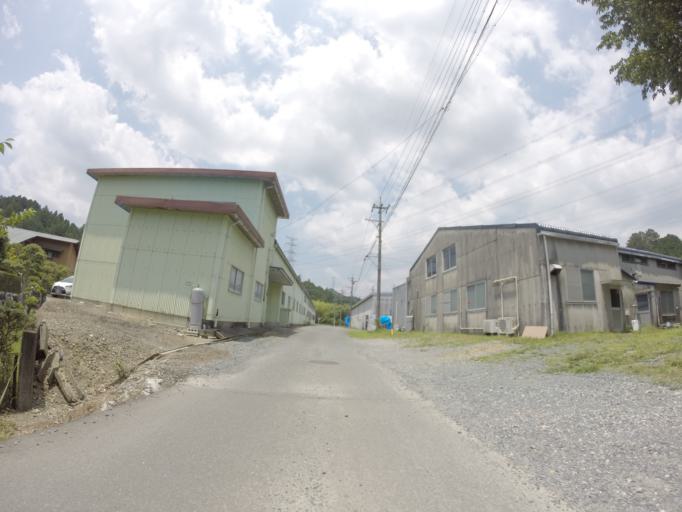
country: JP
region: Shizuoka
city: Kanaya
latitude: 34.8076
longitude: 138.0723
